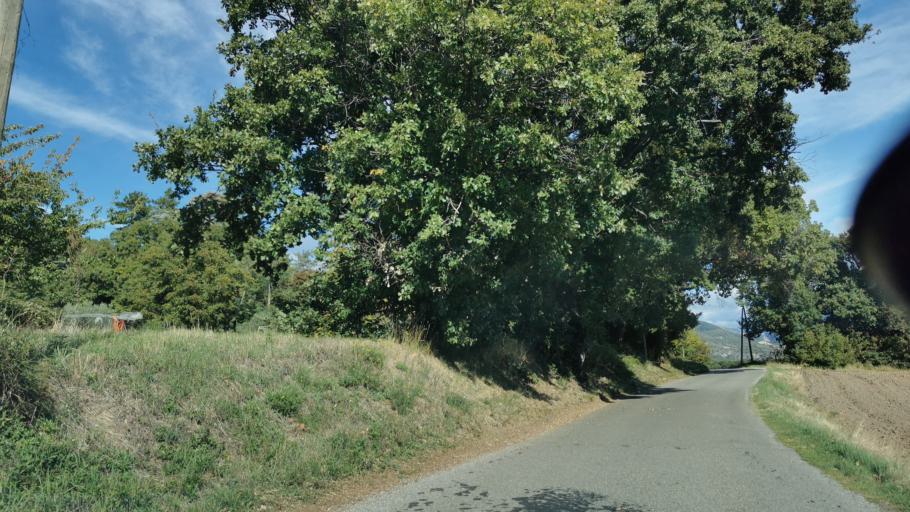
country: FR
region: Provence-Alpes-Cote d'Azur
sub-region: Departement des Alpes-de-Haute-Provence
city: Sisteron
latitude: 44.1721
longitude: 5.9686
